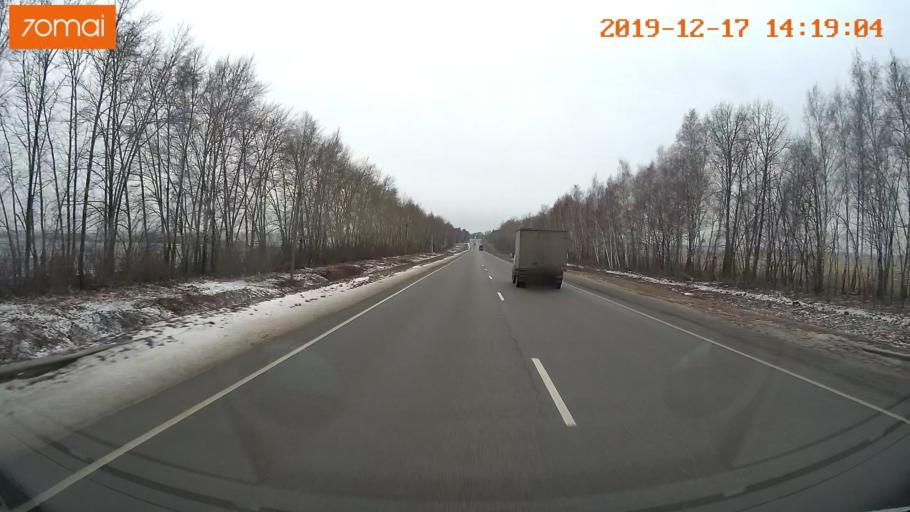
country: RU
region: Rjazan
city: Zakharovo
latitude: 54.4538
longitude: 39.4304
